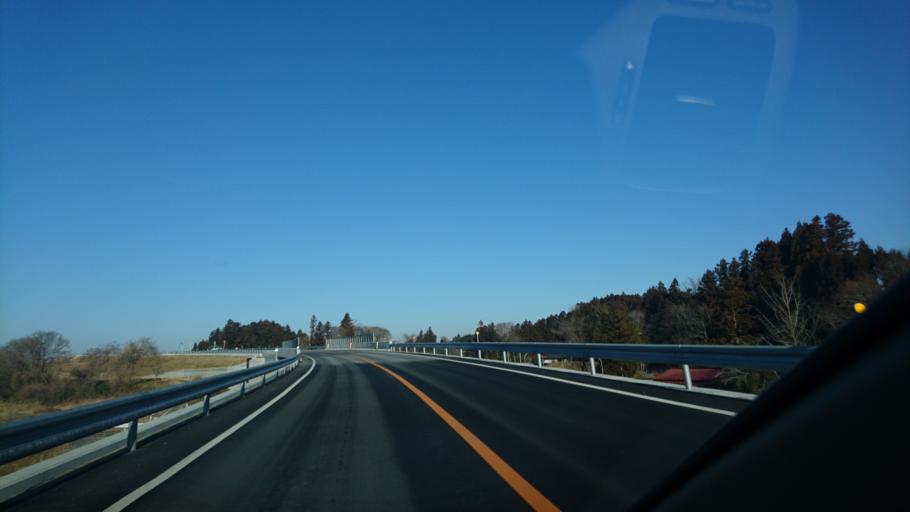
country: JP
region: Miyagi
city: Kogota
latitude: 38.7352
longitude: 141.0523
